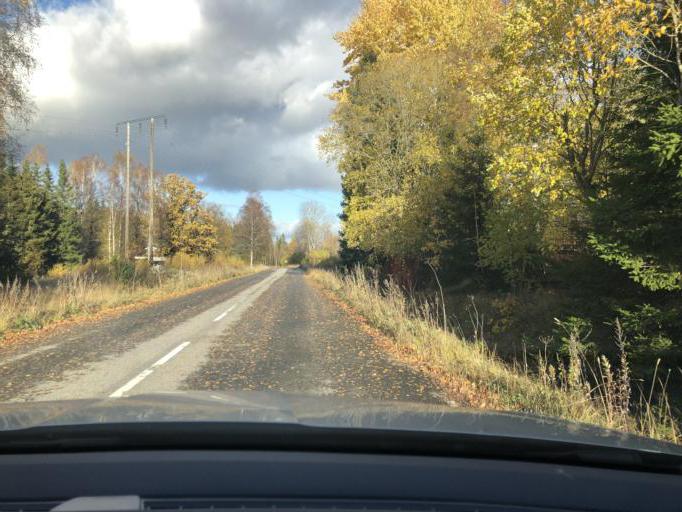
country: SE
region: Vaestra Goetaland
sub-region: Ulricehamns Kommun
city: Ulricehamn
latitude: 57.8152
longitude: 13.2905
